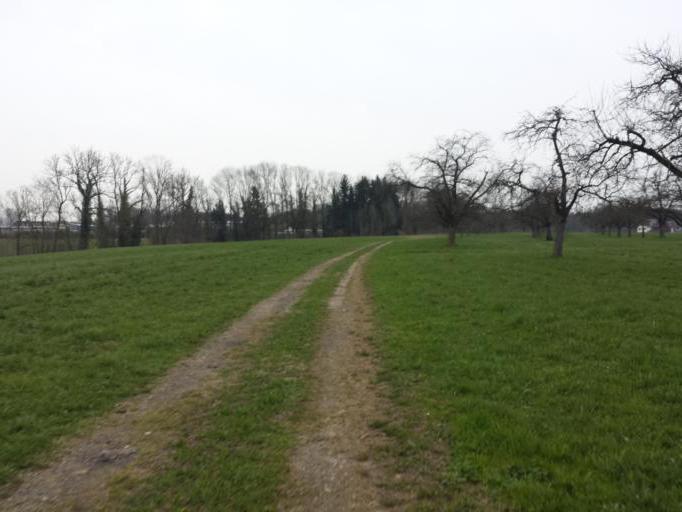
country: CH
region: Saint Gallen
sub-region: Wahlkreis St. Gallen
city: Muolen
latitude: 47.5522
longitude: 9.3330
